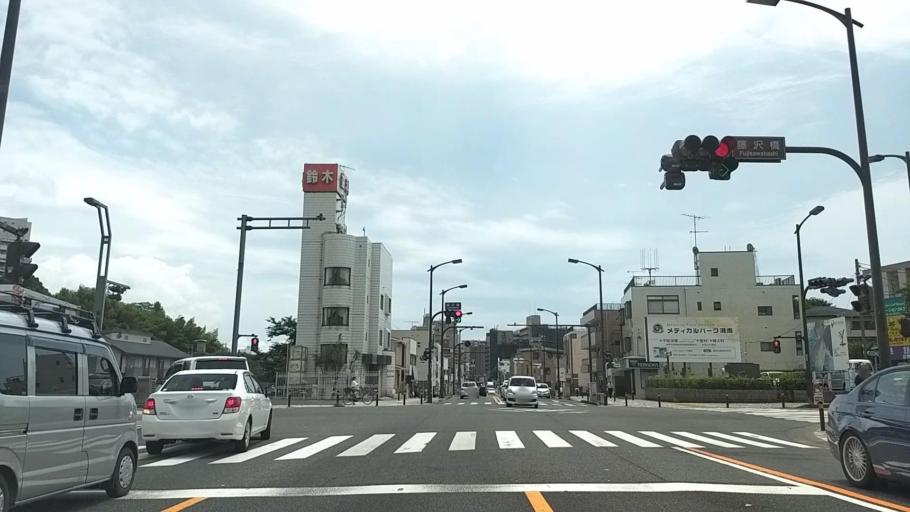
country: JP
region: Kanagawa
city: Fujisawa
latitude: 35.3458
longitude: 139.4867
